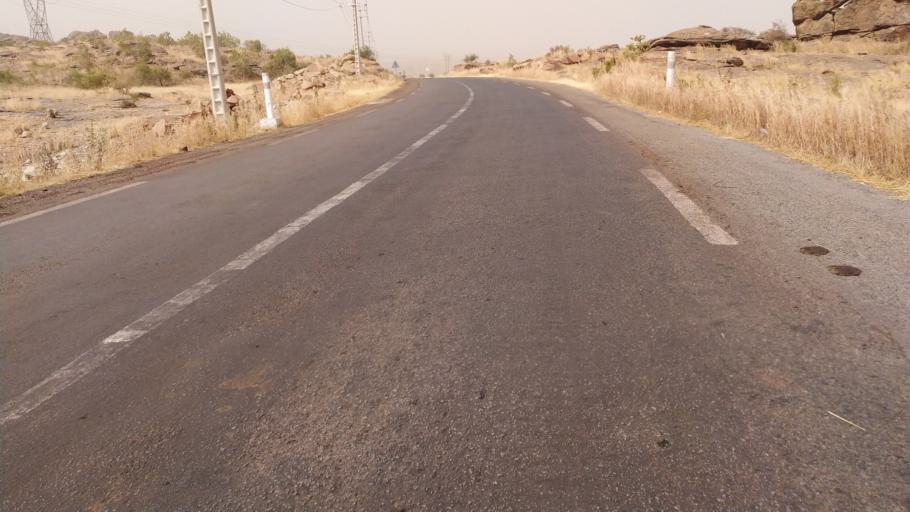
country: ML
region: Kayes
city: Kayes
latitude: 14.3670
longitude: -11.3623
